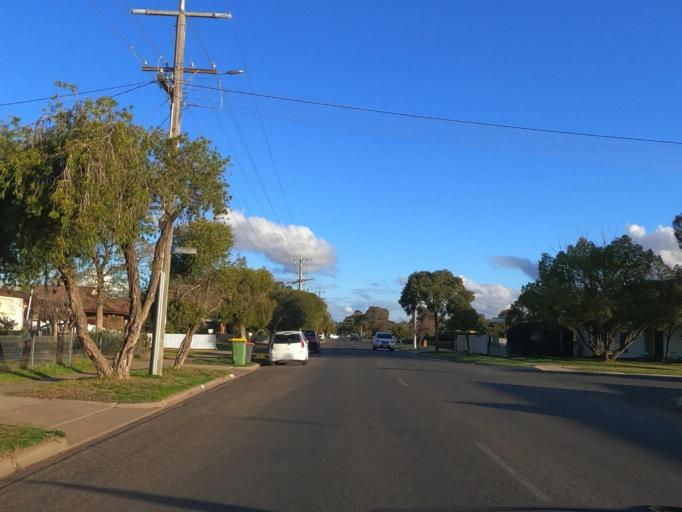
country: AU
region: Victoria
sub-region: Swan Hill
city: Swan Hill
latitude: -35.3414
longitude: 143.5440
